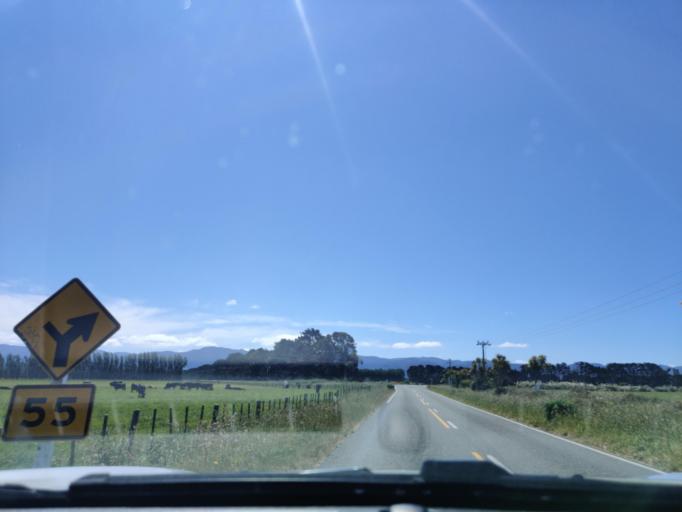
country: NZ
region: Wellington
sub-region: Upper Hutt City
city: Upper Hutt
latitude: -41.2827
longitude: 175.2666
